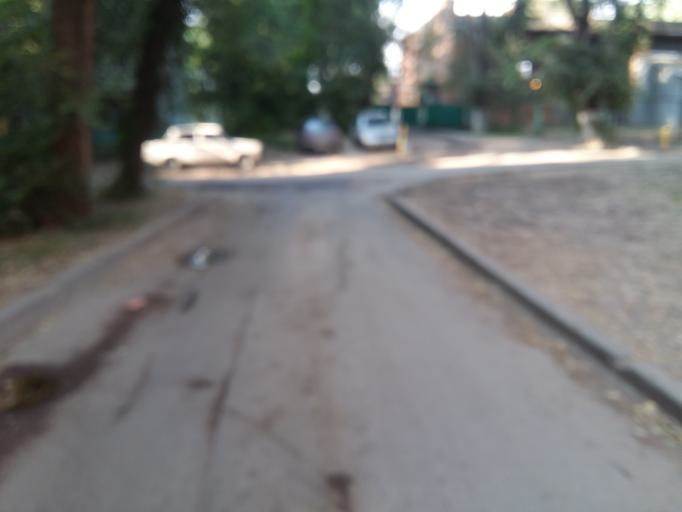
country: RU
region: Rostov
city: Imeni Chkalova
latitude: 47.2772
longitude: 39.7385
